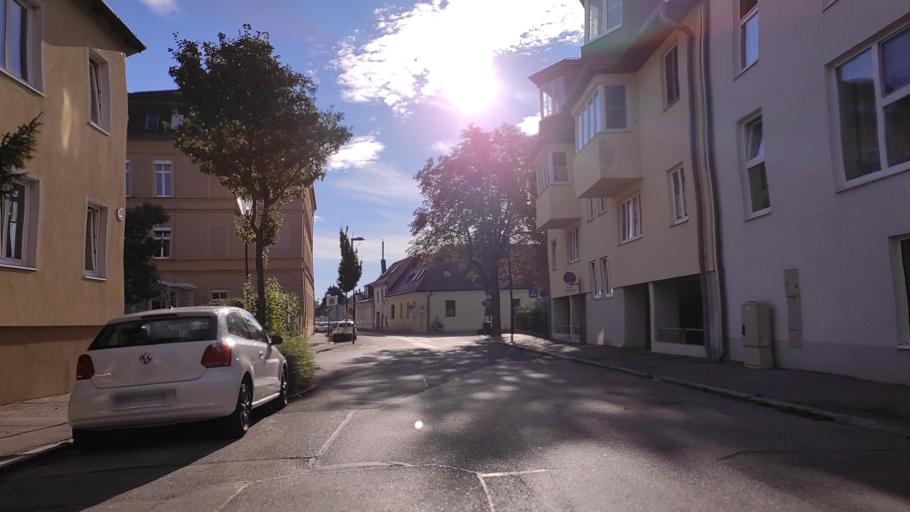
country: AT
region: Lower Austria
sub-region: Politischer Bezirk Baden
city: Baden
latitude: 48.0023
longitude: 16.2472
